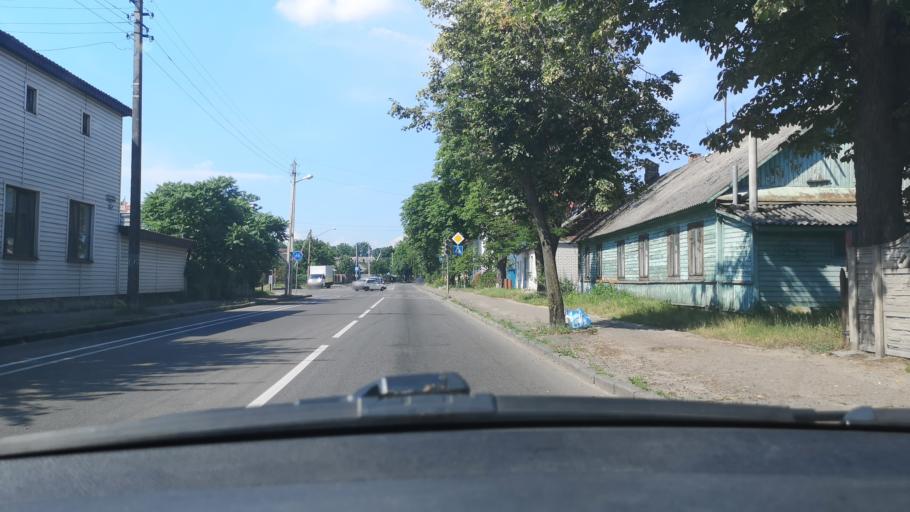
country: BY
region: Brest
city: Brest
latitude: 52.1040
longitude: 23.7108
